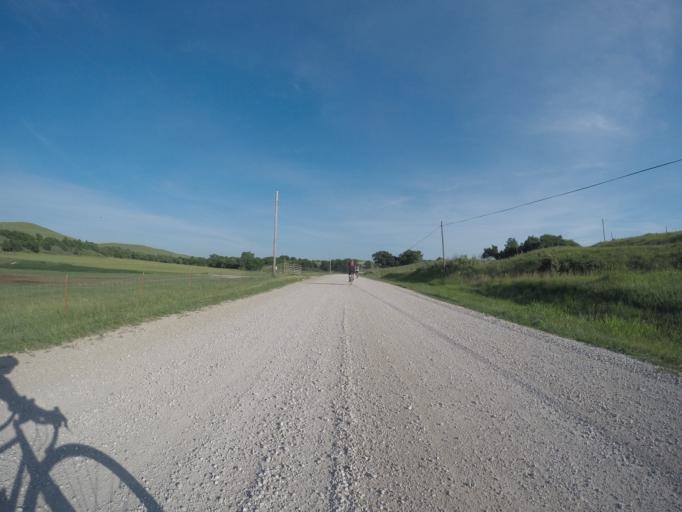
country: US
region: Kansas
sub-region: Riley County
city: Manhattan
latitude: 39.0607
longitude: -96.4989
